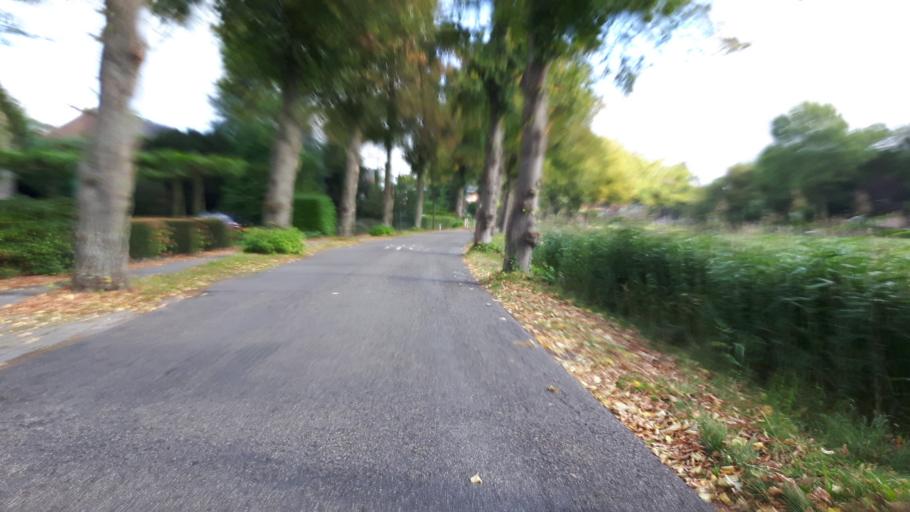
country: NL
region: Utrecht
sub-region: Gemeente Montfoort
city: Montfoort
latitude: 52.0952
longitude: 4.9639
